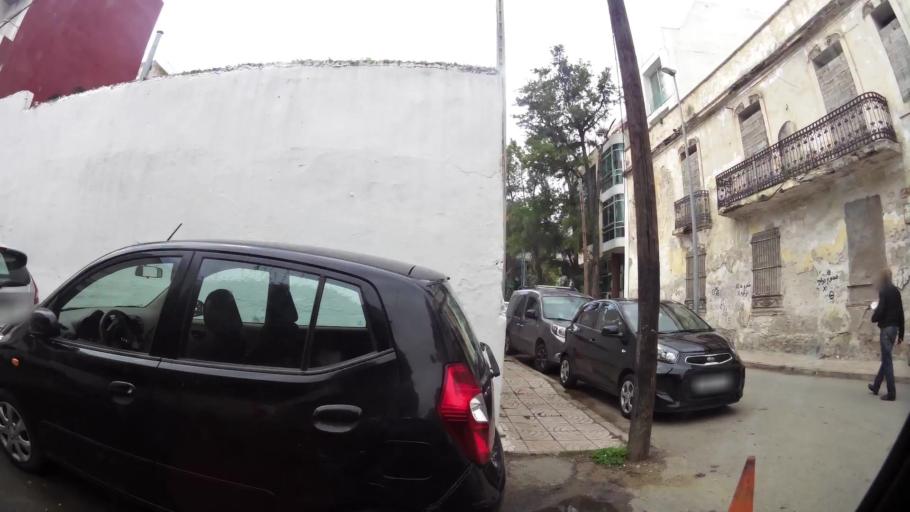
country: MA
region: Grand Casablanca
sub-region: Casablanca
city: Casablanca
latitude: 33.5935
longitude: -7.6267
